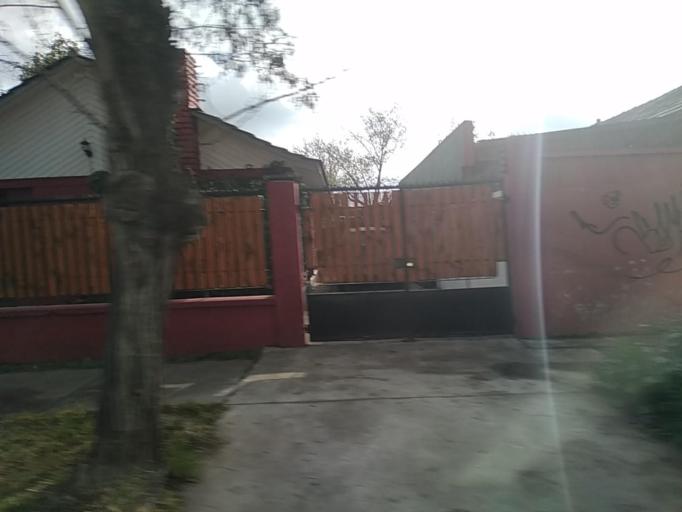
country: CL
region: Santiago Metropolitan
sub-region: Provincia de Santiago
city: Villa Presidente Frei, Nunoa, Santiago, Chile
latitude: -33.4912
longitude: -70.5982
